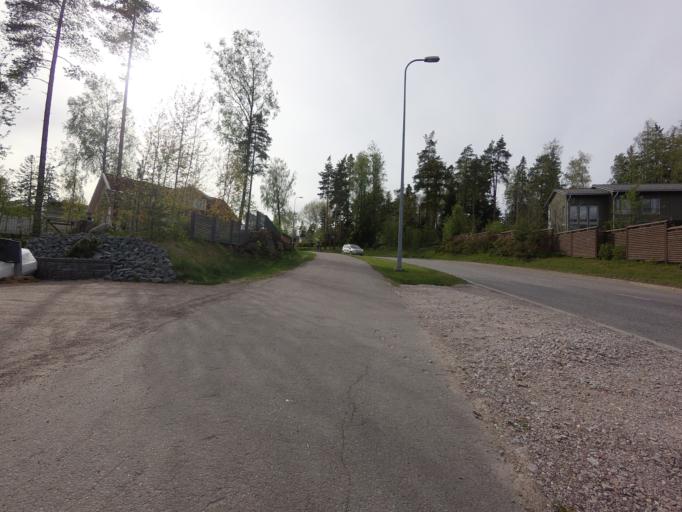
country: FI
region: Uusimaa
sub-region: Helsinki
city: Kauniainen
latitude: 60.1984
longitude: 24.7131
